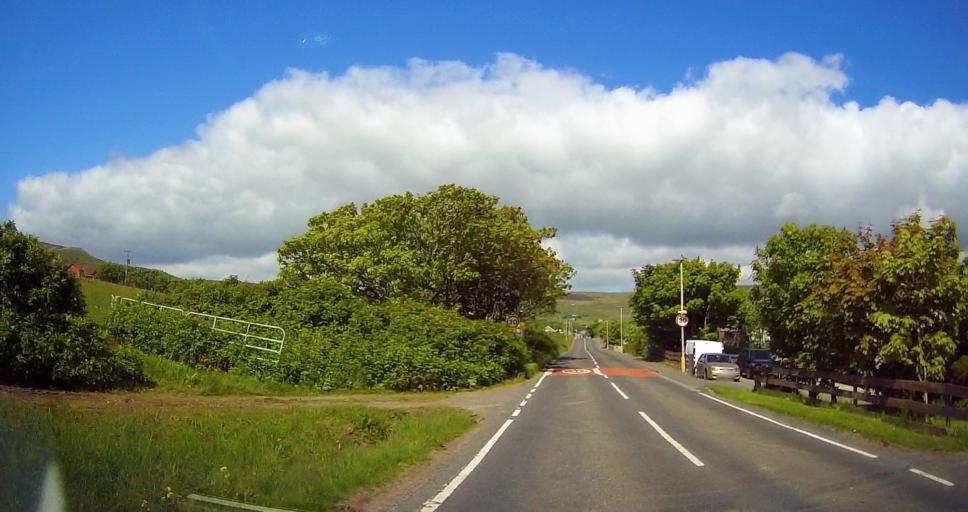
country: GB
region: Scotland
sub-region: Orkney Islands
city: Orkney
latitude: 59.0011
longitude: -3.1051
